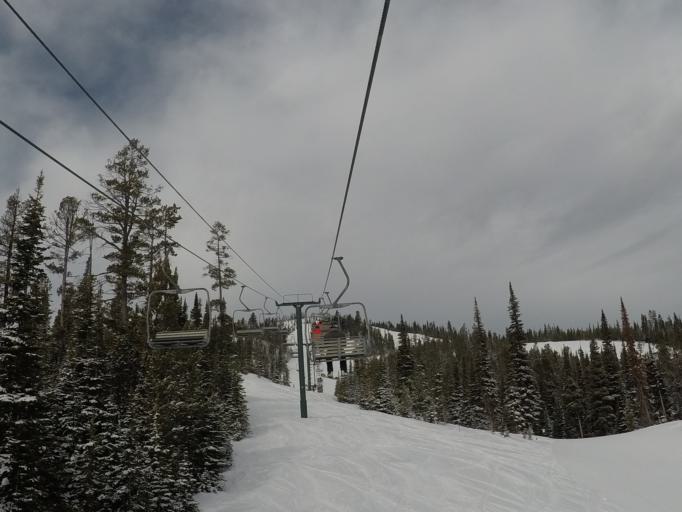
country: US
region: Montana
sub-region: Meagher County
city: White Sulphur Springs
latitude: 46.8365
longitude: -110.7047
